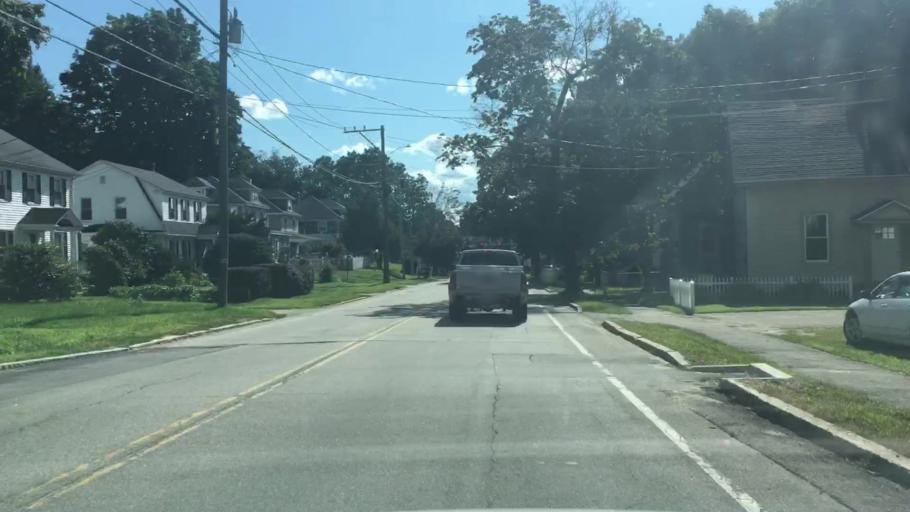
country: US
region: New Hampshire
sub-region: Strafford County
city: Dover
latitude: 43.1836
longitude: -70.8741
